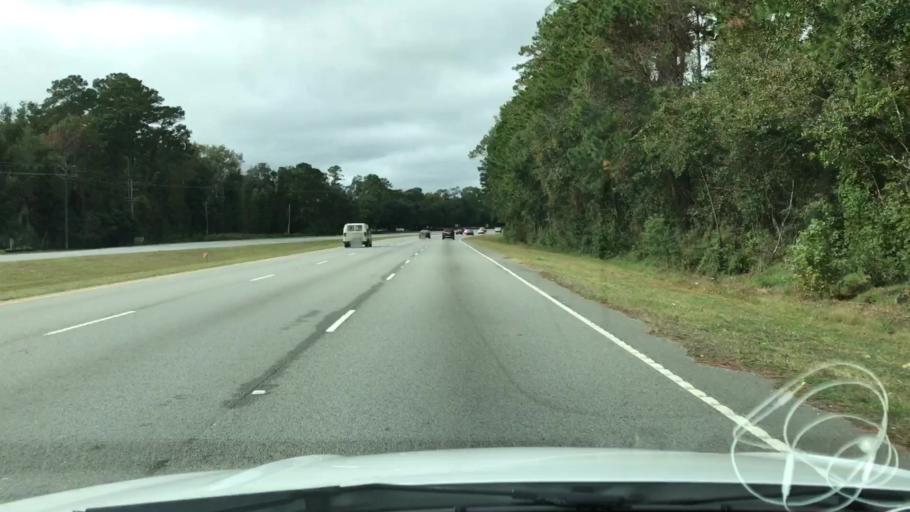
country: US
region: South Carolina
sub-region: Beaufort County
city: Bluffton
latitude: 32.2731
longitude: -80.8675
